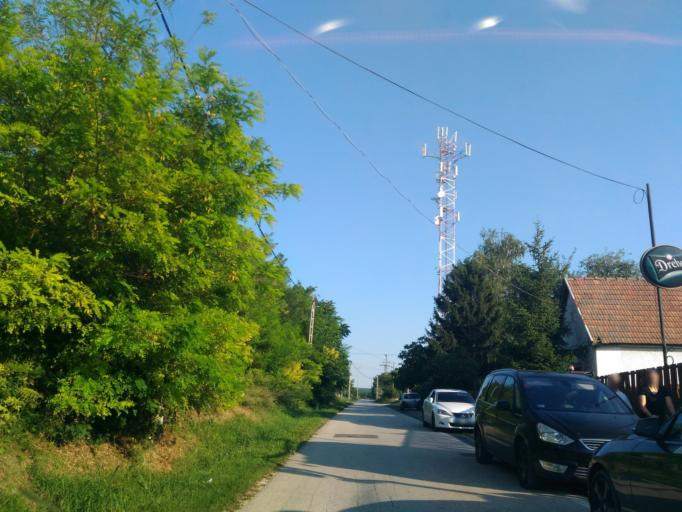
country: HU
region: Somogy
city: Balatonszarszo
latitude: 46.8008
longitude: 17.7848
